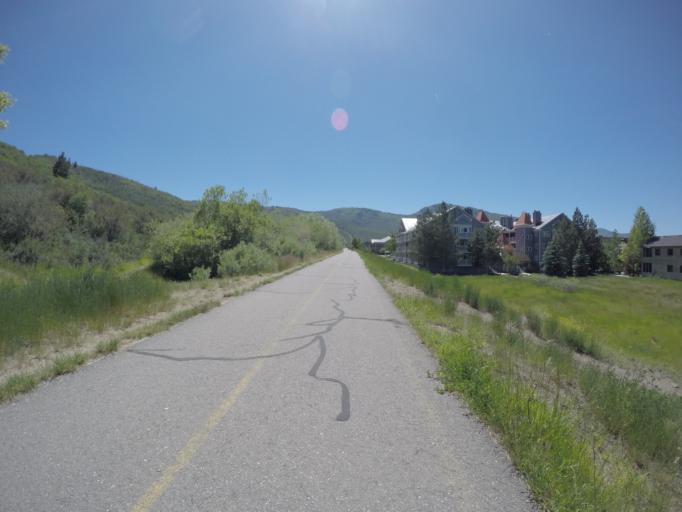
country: US
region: Utah
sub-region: Summit County
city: Park City
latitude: 40.6619
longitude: -111.4963
